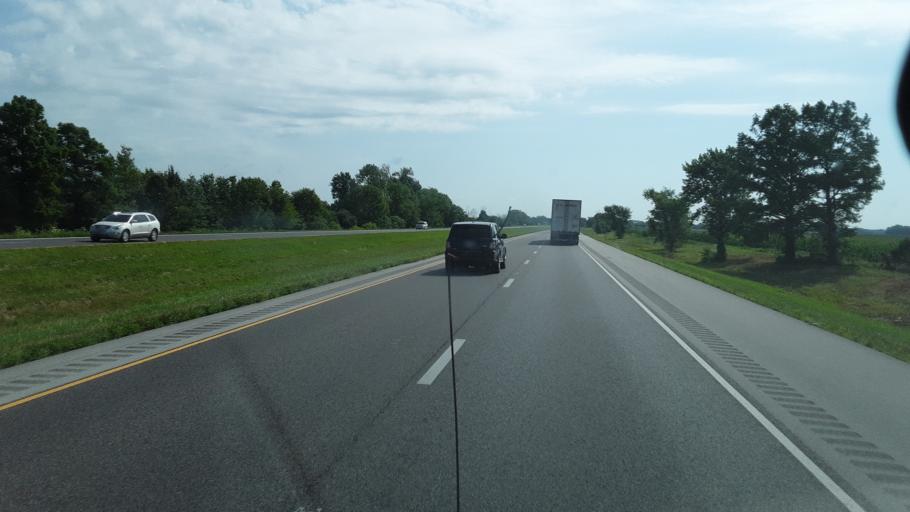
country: US
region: Illinois
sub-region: Fayette County
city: Saint Elmo
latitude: 38.9925
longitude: -88.9240
